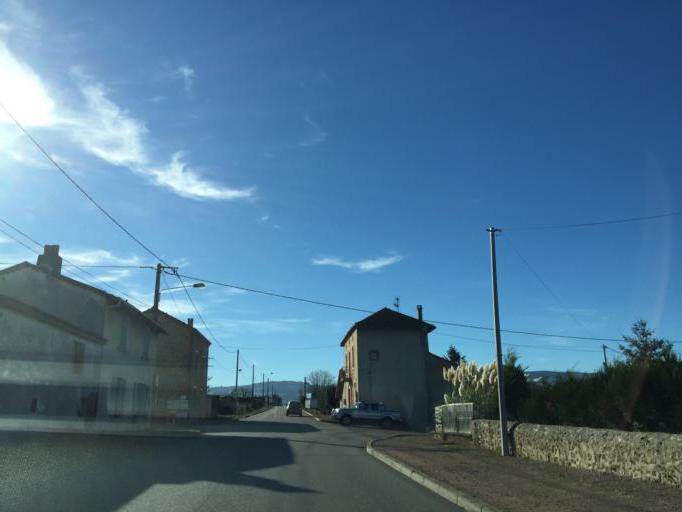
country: FR
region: Rhone-Alpes
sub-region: Departement de la Loire
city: Villerest
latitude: 46.0056
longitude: 4.0138
